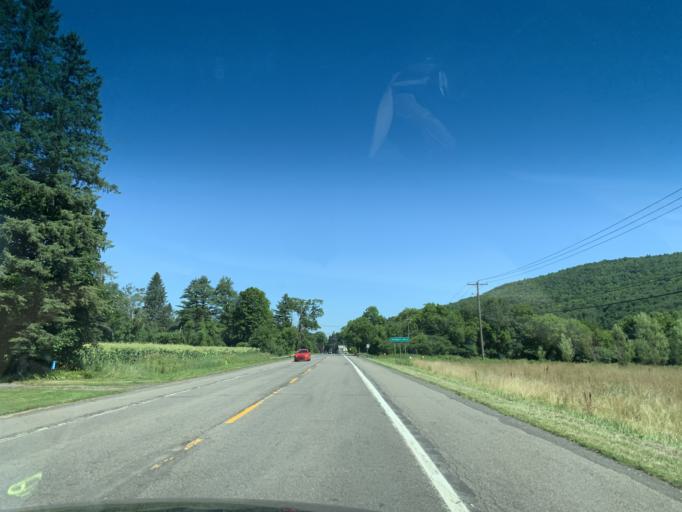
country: US
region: New York
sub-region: Delaware County
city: Sidney
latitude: 42.4430
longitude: -75.3877
